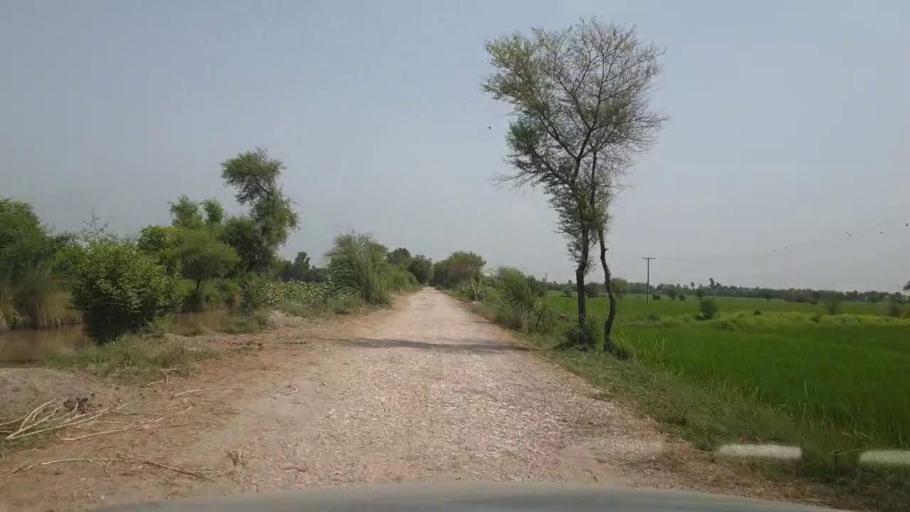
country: PK
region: Sindh
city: Garhi Yasin
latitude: 27.9467
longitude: 68.3755
